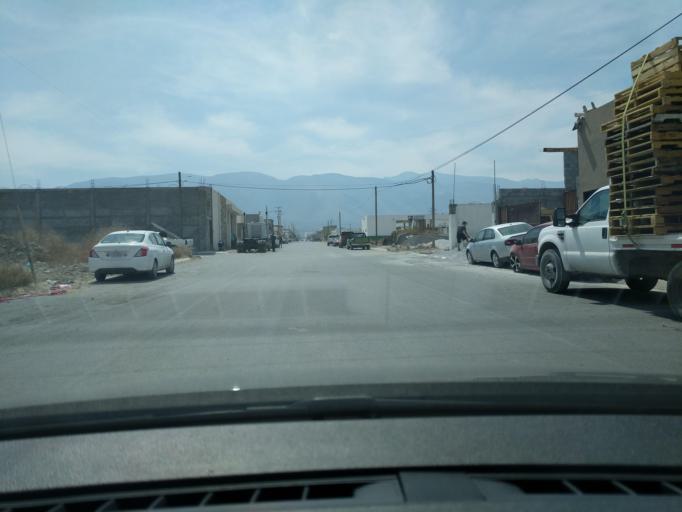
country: MX
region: Coahuila
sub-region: Arteaga
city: Arteaga
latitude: 25.4325
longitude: -100.9102
